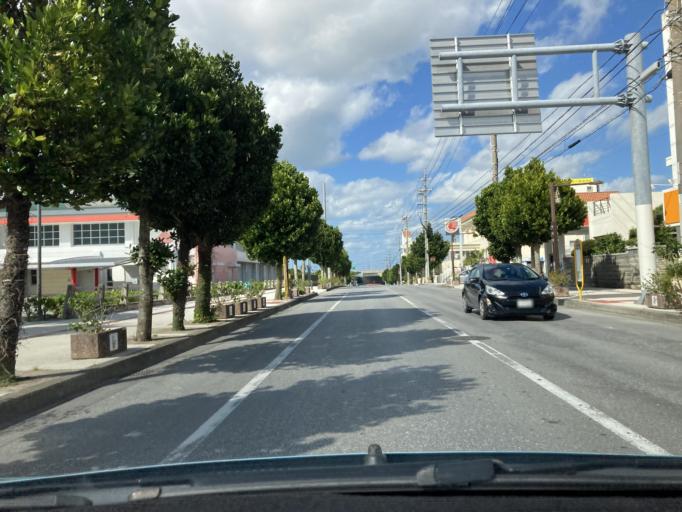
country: JP
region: Okinawa
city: Okinawa
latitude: 26.3336
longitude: 127.7909
